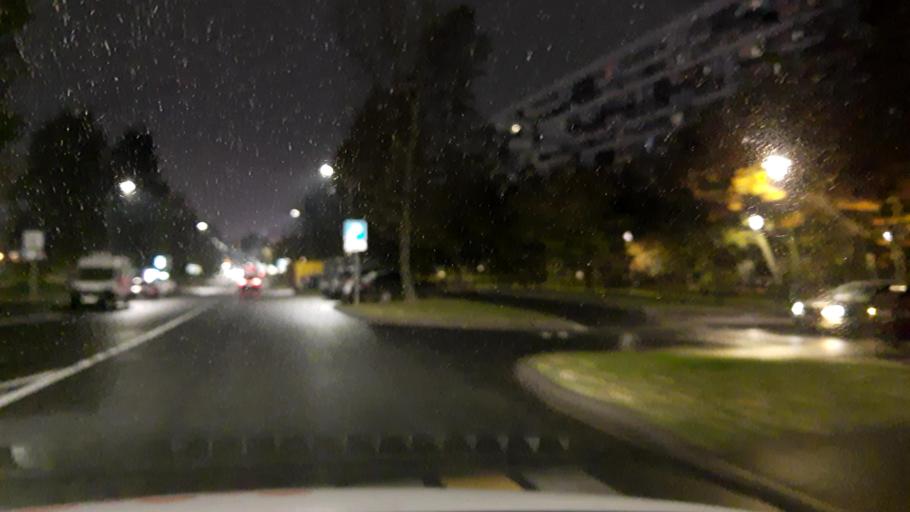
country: RU
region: Moskovskaya
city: Alekseyevka
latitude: 55.6322
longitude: 37.8031
